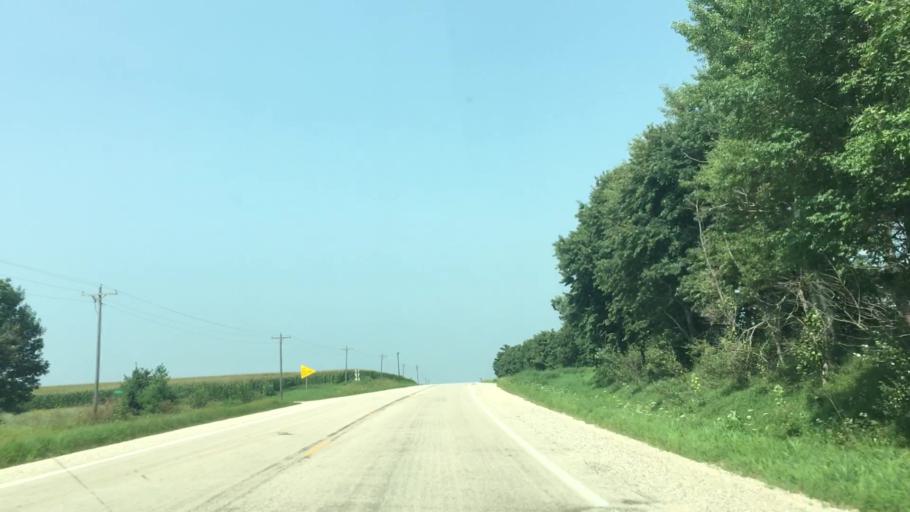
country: US
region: Iowa
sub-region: Fayette County
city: West Union
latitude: 43.0048
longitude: -91.8245
